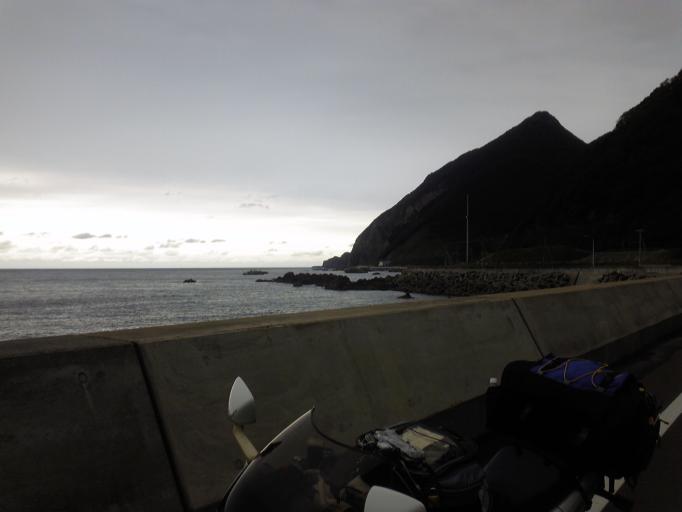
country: JP
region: Hokkaido
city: Kamiiso
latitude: 42.2742
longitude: 139.7856
